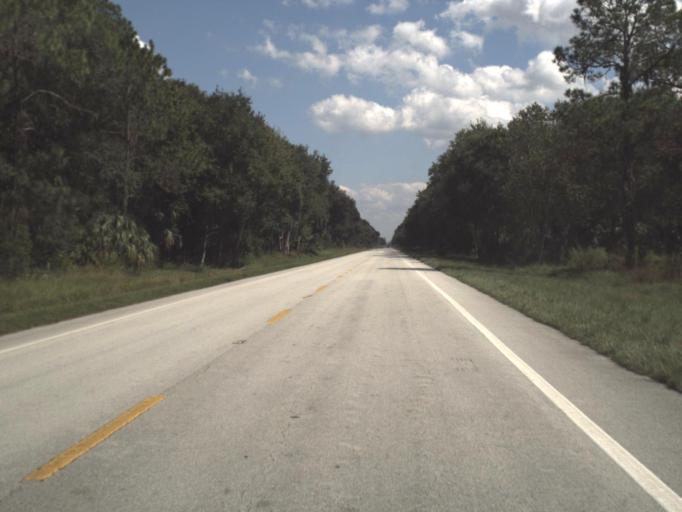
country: US
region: Florida
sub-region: Highlands County
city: Sebring
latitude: 27.4123
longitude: -81.5513
